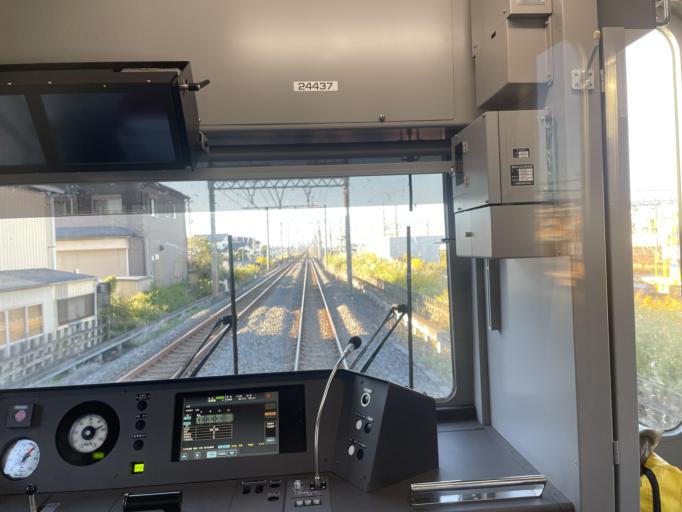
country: JP
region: Saitama
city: Kurihashi
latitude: 36.1206
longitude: 139.7041
